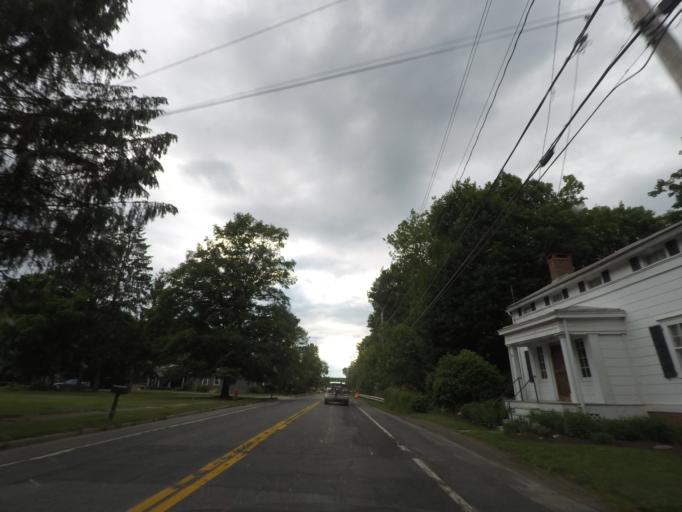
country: US
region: New York
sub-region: Dutchess County
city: Pine Plains
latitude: 41.9783
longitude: -73.6498
